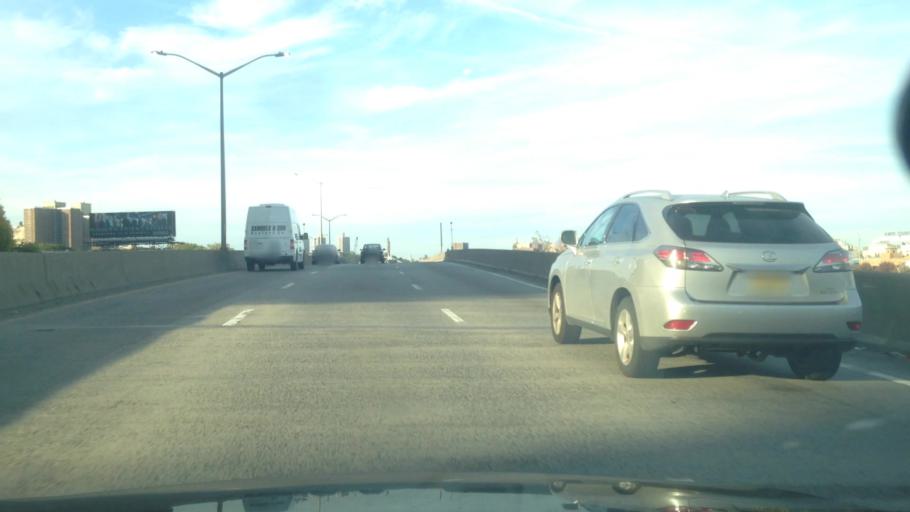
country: US
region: New Jersey
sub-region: Bergen County
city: Edgewater
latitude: 40.8212
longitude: -73.9344
